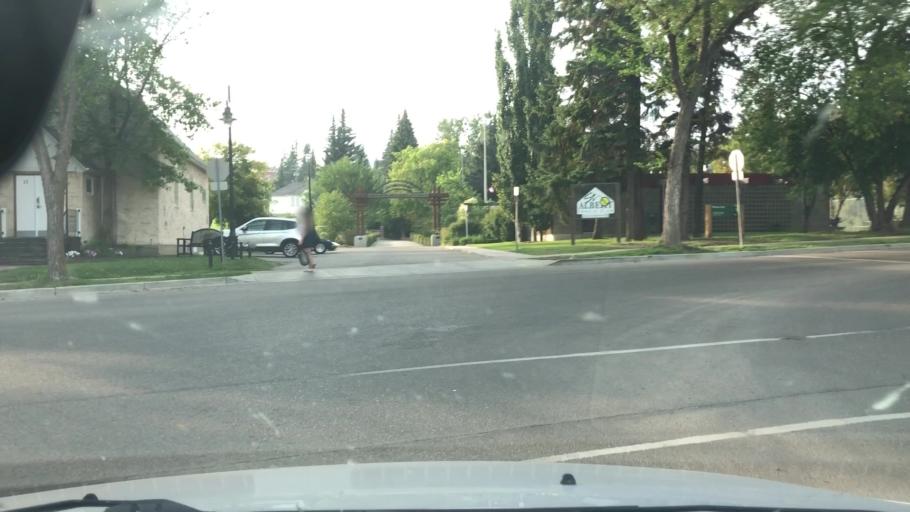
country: CA
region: Alberta
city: St. Albert
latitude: 53.6361
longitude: -113.6277
